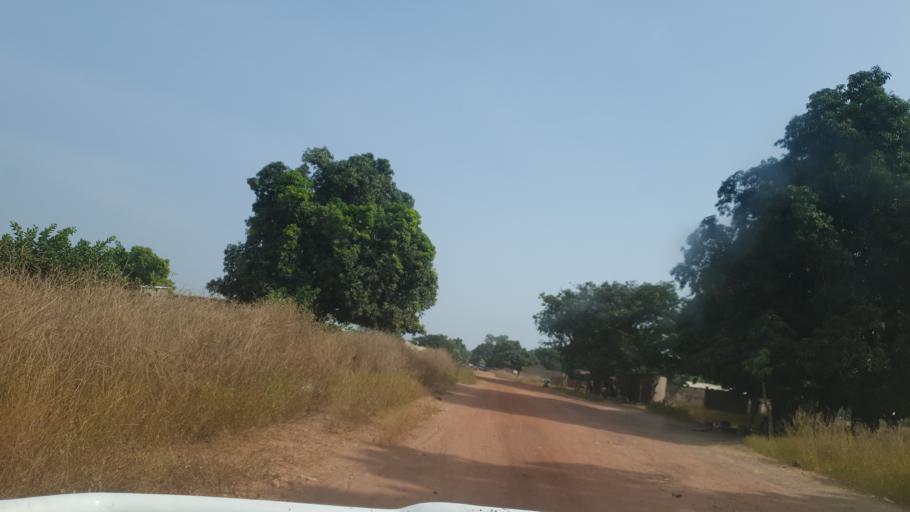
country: ML
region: Koulikoro
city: Dioila
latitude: 12.2204
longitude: -6.2104
